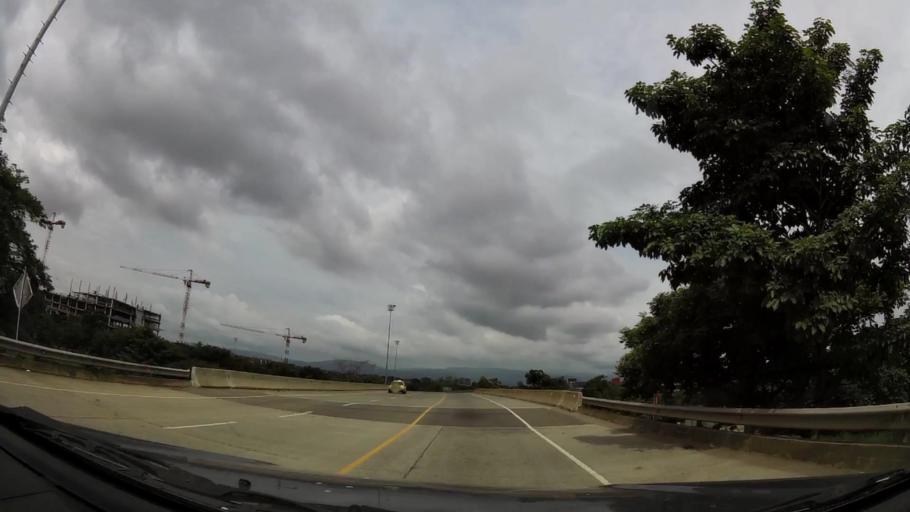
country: PA
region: Panama
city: San Miguelito
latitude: 9.0370
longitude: -79.4210
